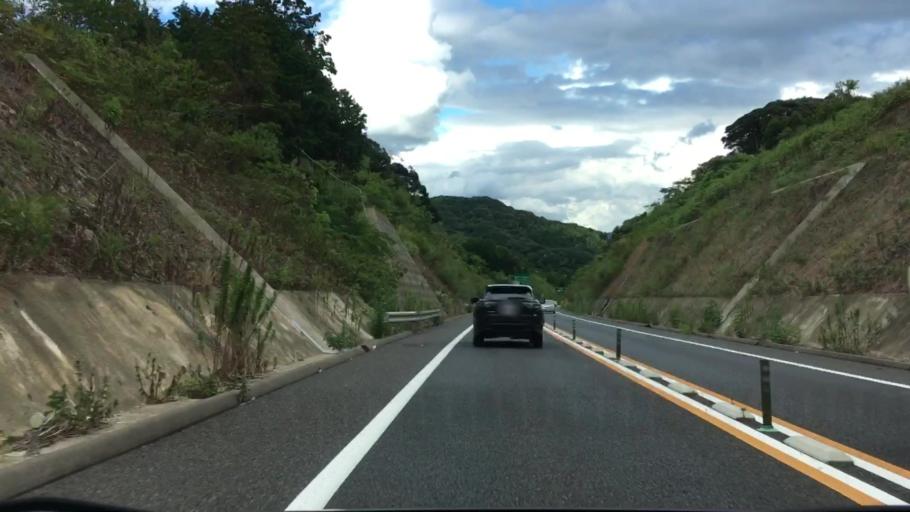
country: JP
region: Saga Prefecture
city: Karatsu
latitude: 33.4027
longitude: 129.9467
